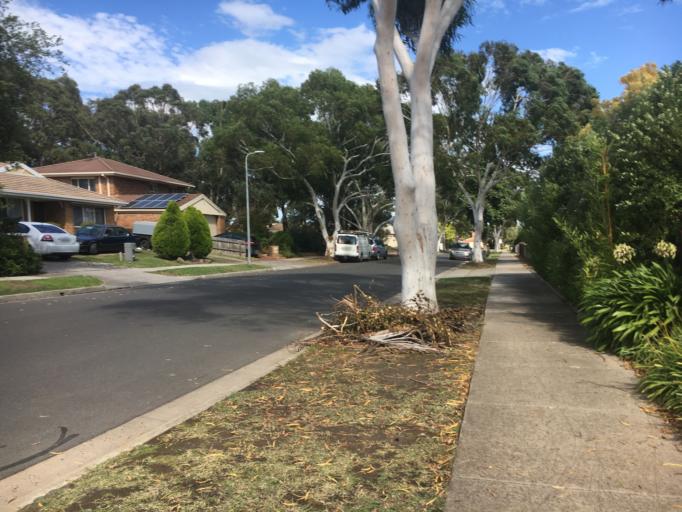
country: AU
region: Victoria
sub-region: Knox
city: Ferntree Gully
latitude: -37.8919
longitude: 145.2766
